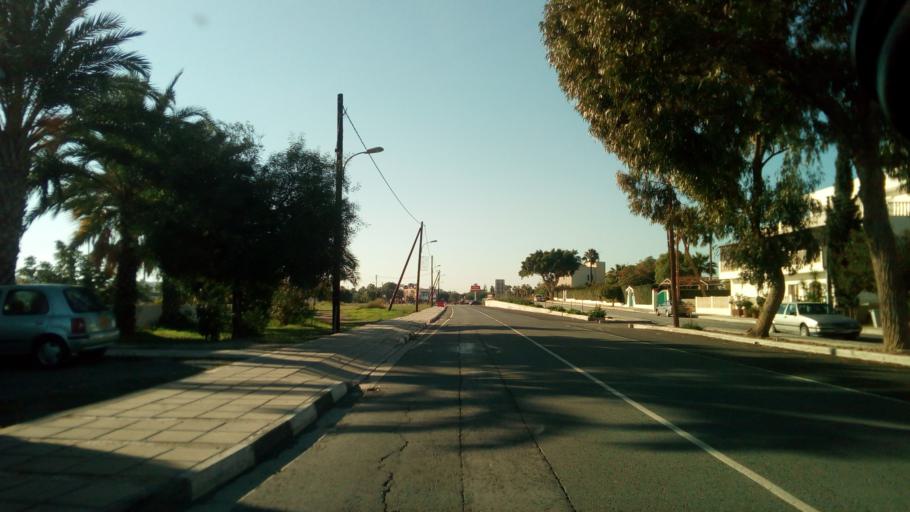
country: CY
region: Larnaka
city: Voroklini
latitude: 34.9769
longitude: 33.6745
